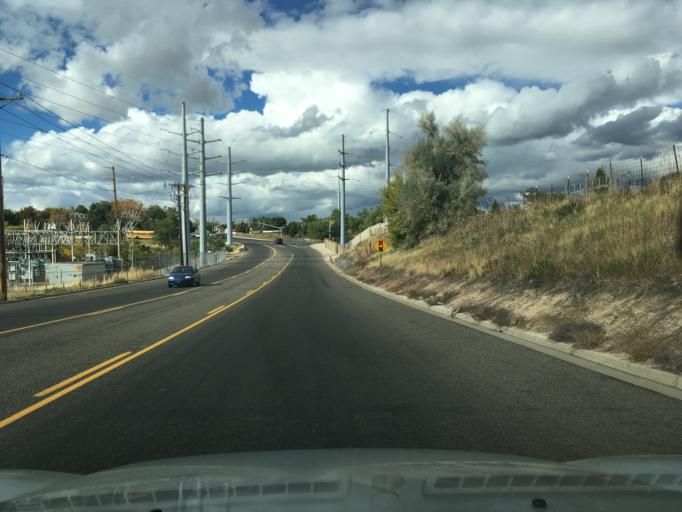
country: US
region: Utah
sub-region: Davis County
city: Layton
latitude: 41.0728
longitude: -111.9577
